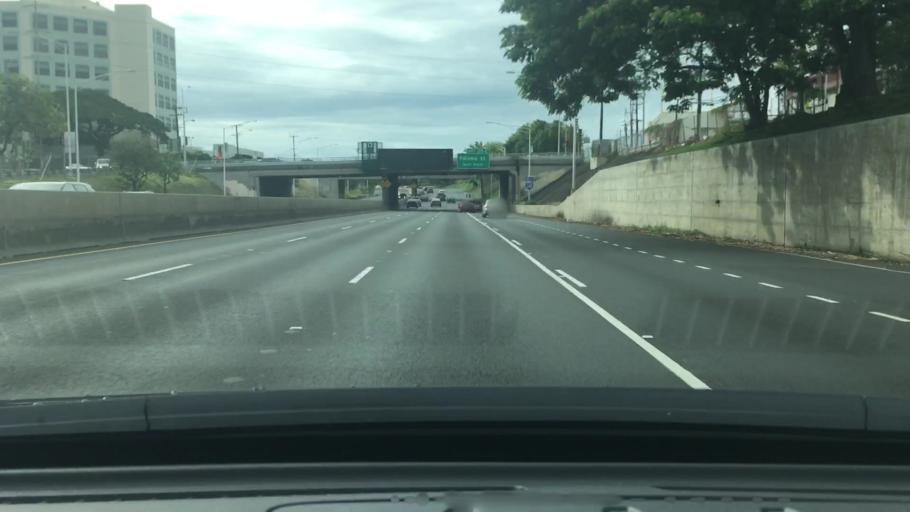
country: US
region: Hawaii
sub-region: Honolulu County
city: Honolulu
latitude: 21.3206
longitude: -157.8595
